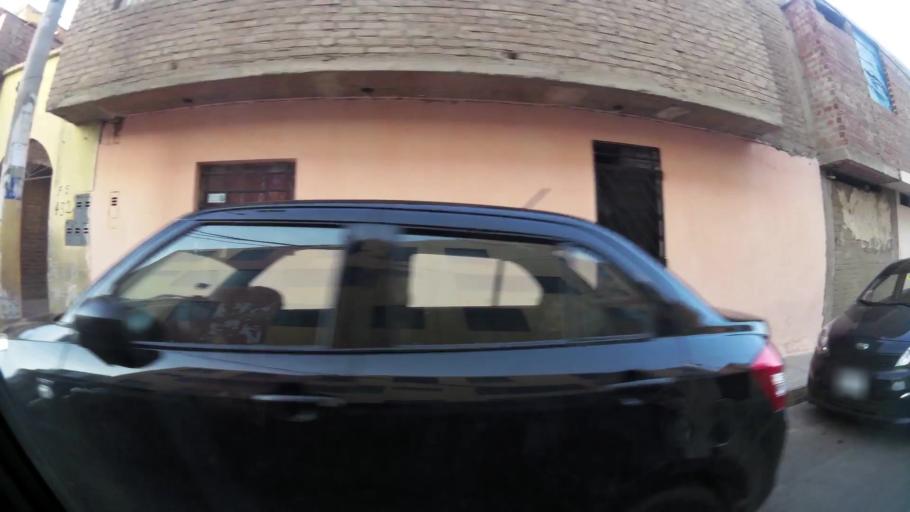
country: PE
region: Lambayeque
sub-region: Provincia de Chiclayo
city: Chiclayo
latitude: -6.7732
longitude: -79.8345
